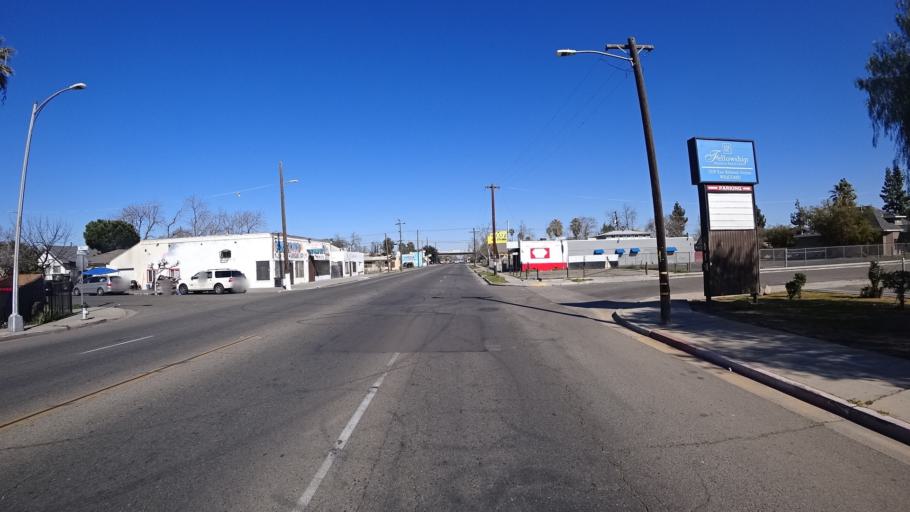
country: US
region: California
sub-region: Fresno County
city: Fresno
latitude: 36.7514
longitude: -119.7815
